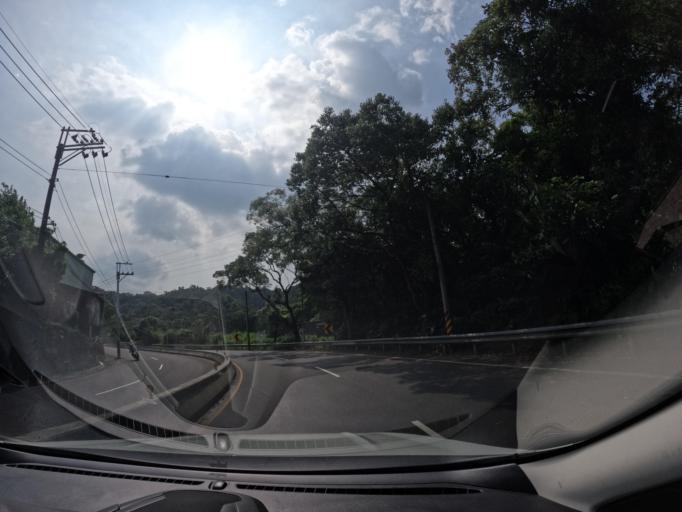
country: TW
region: Taiwan
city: Daxi
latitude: 24.9046
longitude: 121.3469
